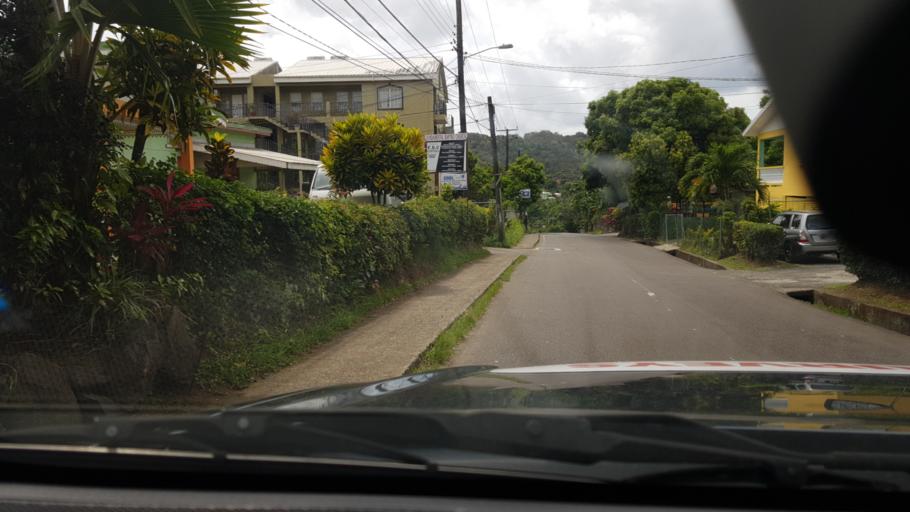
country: LC
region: Castries Quarter
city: Bisee
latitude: 14.0138
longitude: -60.9543
